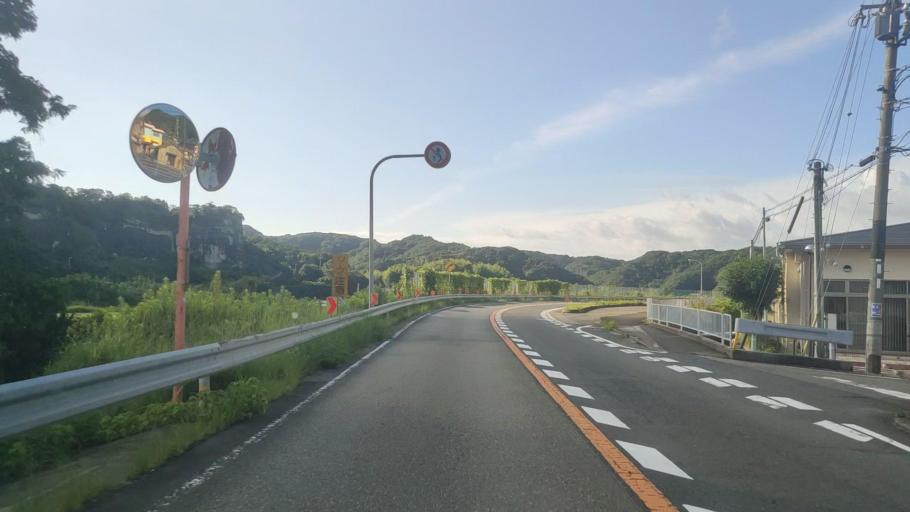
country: JP
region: Wakayama
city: Tanabe
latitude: 33.6617
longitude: 135.3990
